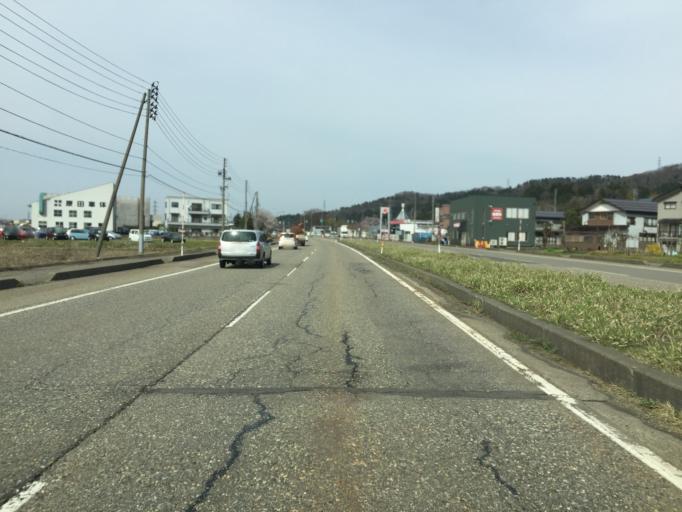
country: JP
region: Niigata
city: Ojiya
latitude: 37.3584
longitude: 138.8314
